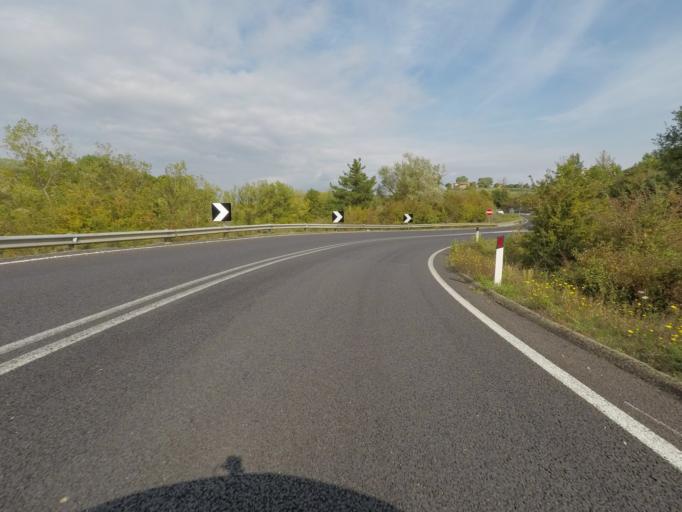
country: IT
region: Tuscany
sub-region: Provincia di Siena
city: Belverde
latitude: 43.3564
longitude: 11.3042
